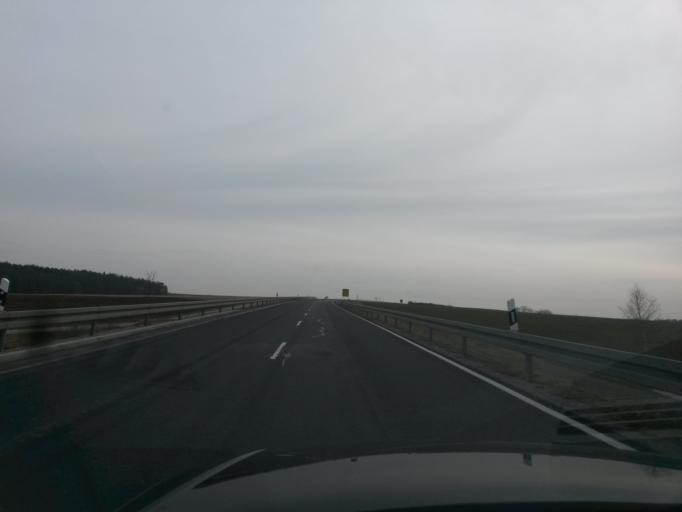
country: DE
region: Bavaria
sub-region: Regierungsbezirk Unterfranken
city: Mellrichstadt
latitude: 50.4297
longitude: 10.3311
